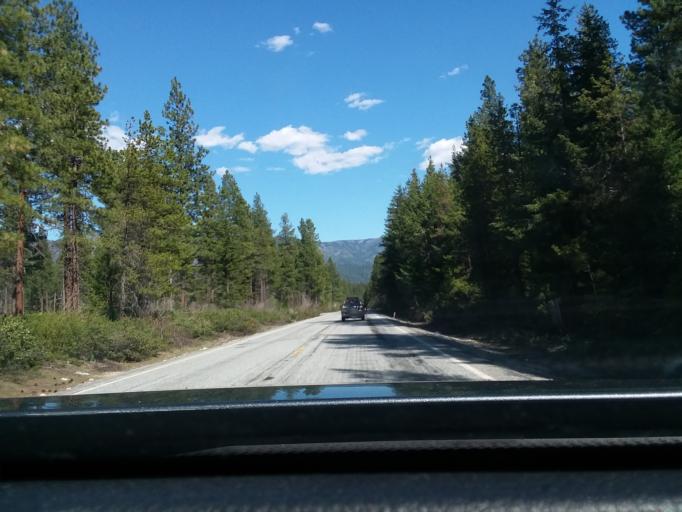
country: US
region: Washington
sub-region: Chelan County
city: Leavenworth
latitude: 47.8019
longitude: -120.6833
